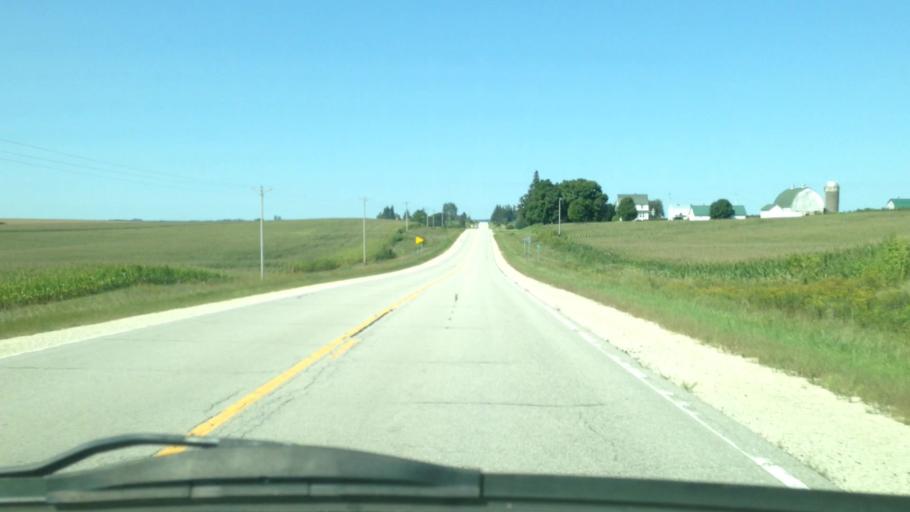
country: US
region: Minnesota
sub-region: Houston County
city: Spring Grove
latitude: 43.6093
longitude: -91.7904
